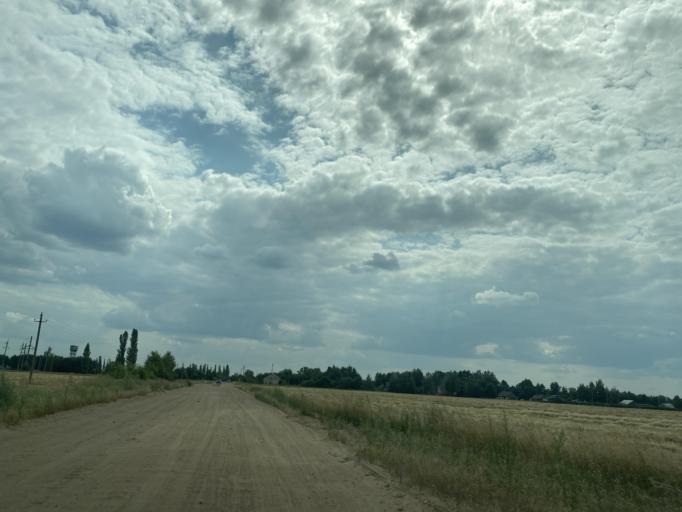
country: BY
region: Brest
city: Ivanava
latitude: 52.3557
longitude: 25.6298
